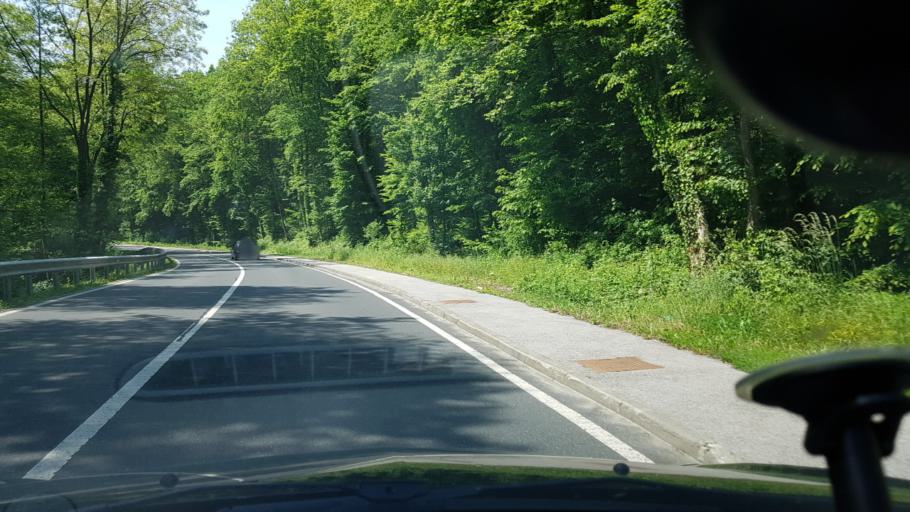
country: HR
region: Krapinsko-Zagorska
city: Marija Bistrica
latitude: 45.9894
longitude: 16.1167
